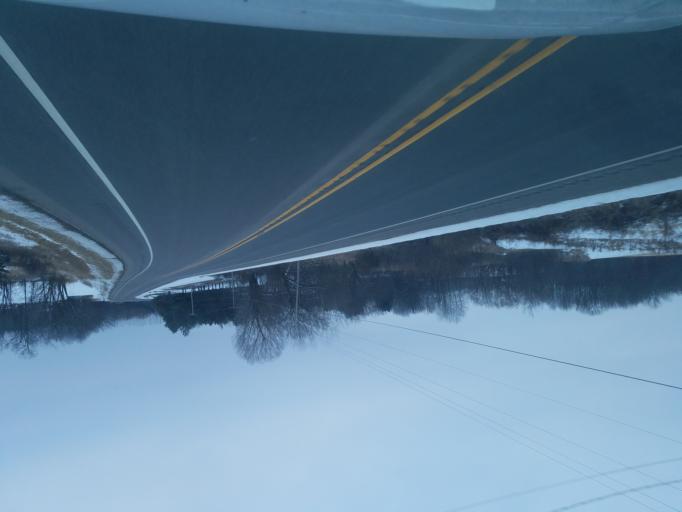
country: US
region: Wisconsin
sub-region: Waupaca County
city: New London
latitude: 44.4110
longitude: -88.8367
